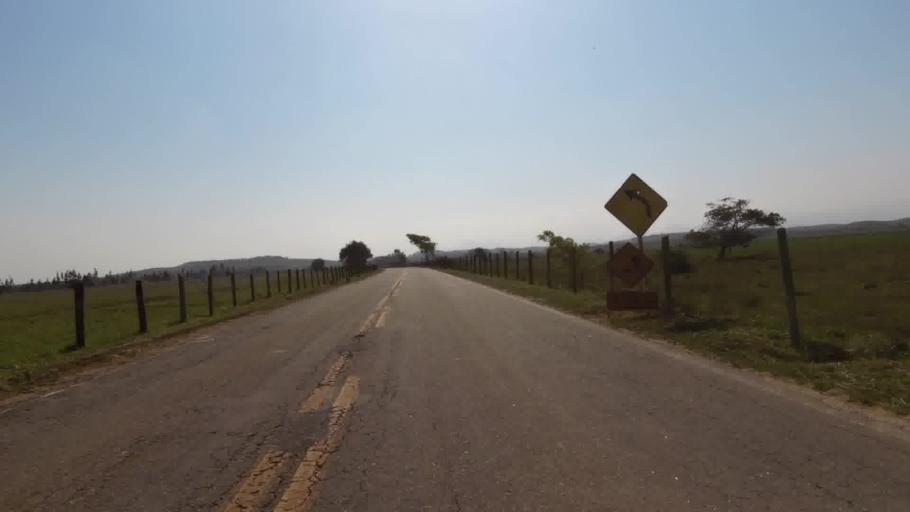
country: BR
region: Espirito Santo
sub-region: Itapemirim
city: Itapemirim
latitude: -20.9881
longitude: -40.8563
